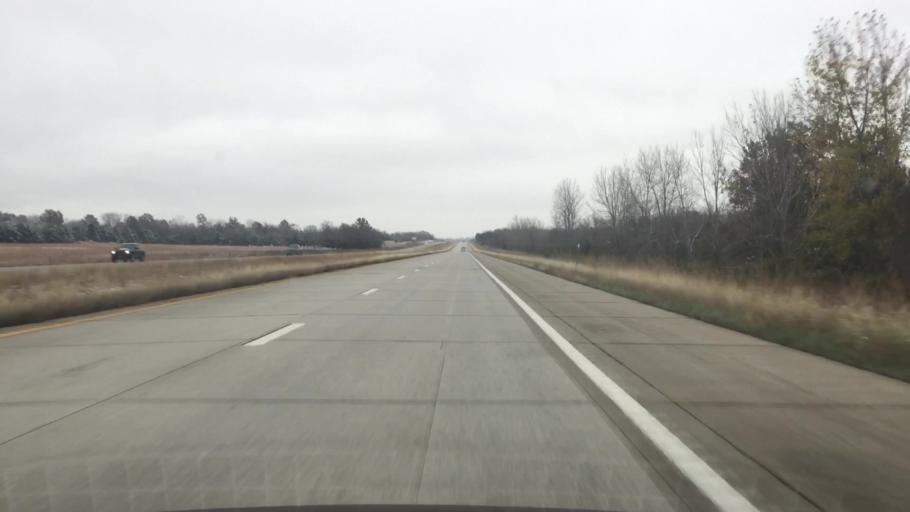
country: US
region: Missouri
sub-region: Henry County
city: Clinton
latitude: 38.2130
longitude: -93.7590
